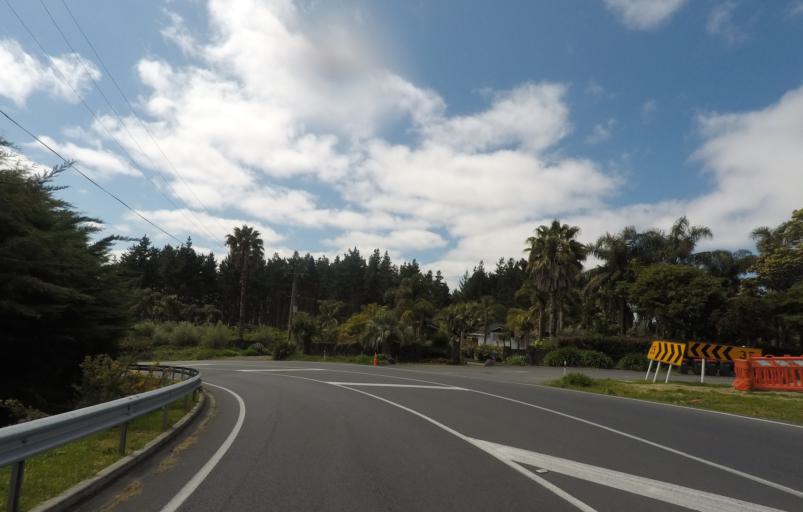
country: NZ
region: Auckland
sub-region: Auckland
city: Manukau City
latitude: -36.9893
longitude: 174.9181
